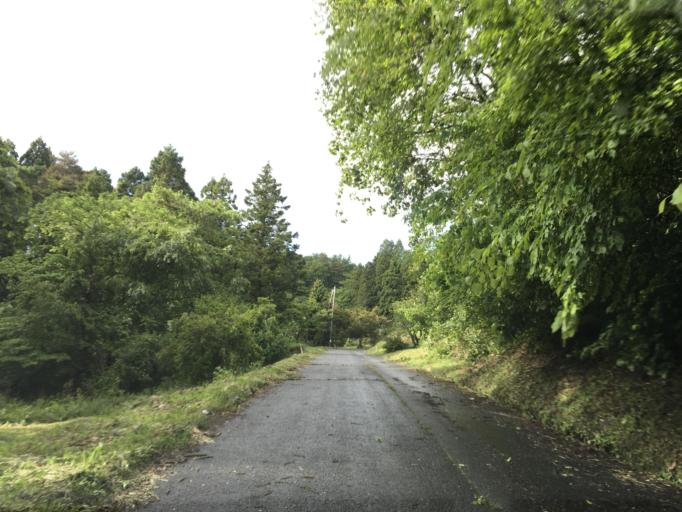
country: JP
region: Iwate
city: Ichinoseki
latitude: 38.8666
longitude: 141.4394
